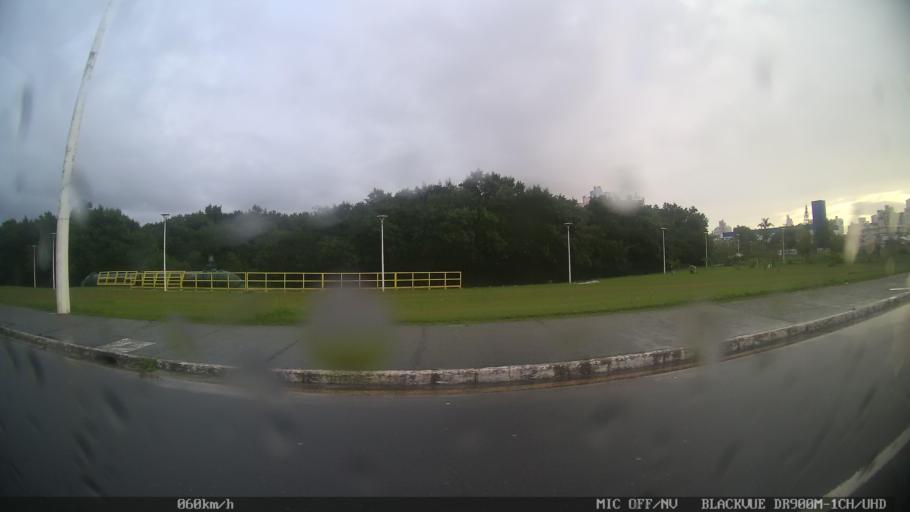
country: BR
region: Santa Catarina
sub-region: Sao Jose
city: Campinas
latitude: -27.6040
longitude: -48.6188
